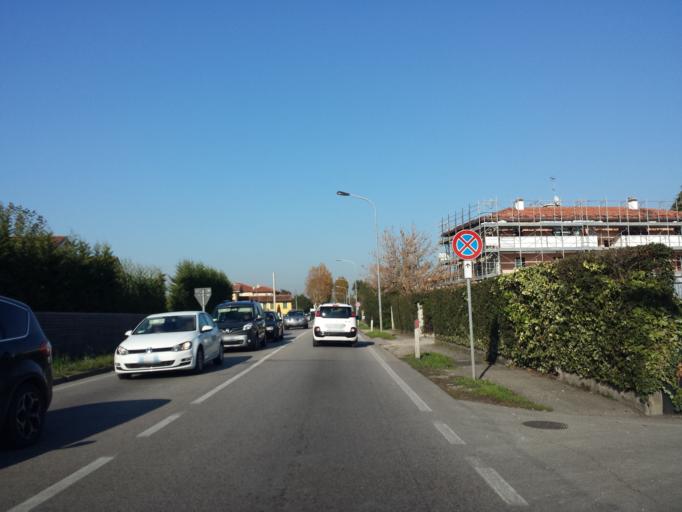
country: IT
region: Veneto
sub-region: Provincia di Treviso
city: Castelfranco Veneto
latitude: 45.6841
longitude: 11.9271
